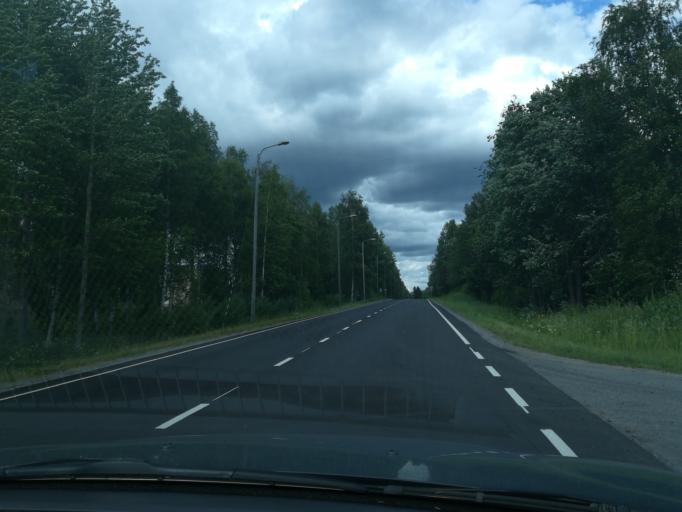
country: FI
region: Southern Savonia
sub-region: Mikkeli
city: Mikkeli
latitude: 61.6442
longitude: 27.0794
